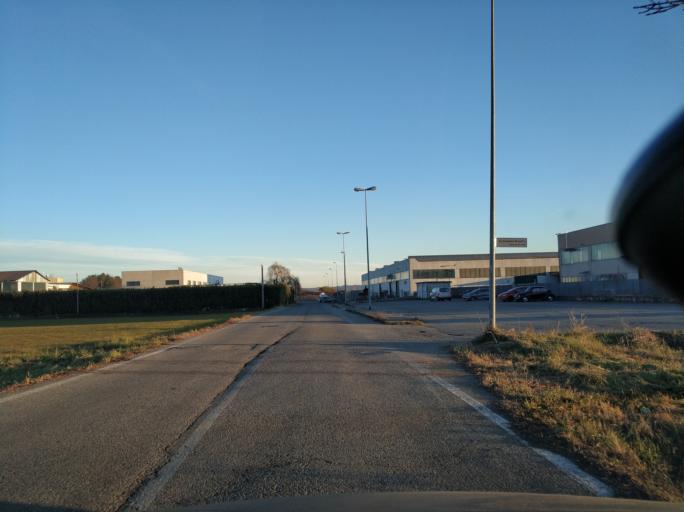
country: IT
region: Piedmont
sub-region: Provincia di Torino
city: San Maurizio
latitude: 45.1939
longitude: 7.6239
